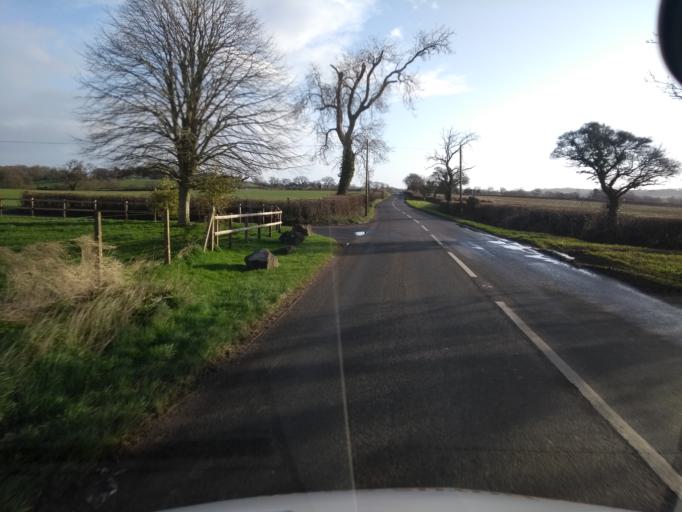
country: GB
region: England
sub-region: Somerset
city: Castle Cary
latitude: 51.0517
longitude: -2.5371
